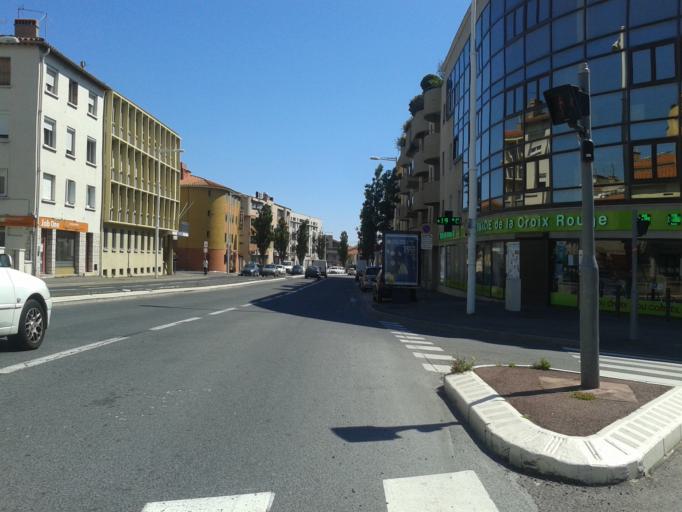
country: FR
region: Languedoc-Roussillon
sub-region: Departement des Pyrenees-Orientales
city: Perpignan
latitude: 42.6911
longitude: 2.8988
